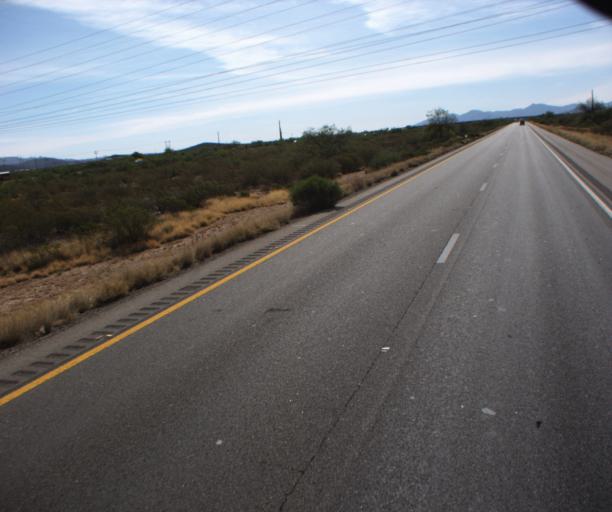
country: US
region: Arizona
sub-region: Pima County
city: Vail
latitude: 32.0327
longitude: -110.7292
